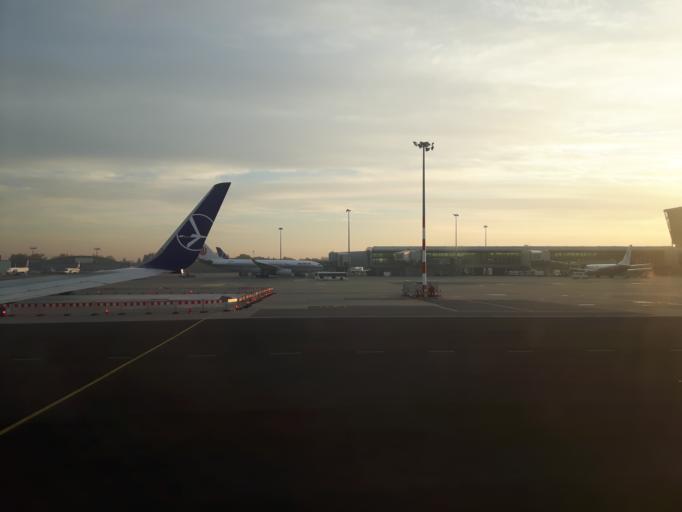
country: PL
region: Masovian Voivodeship
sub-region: Warszawa
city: Wlochy
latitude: 52.1734
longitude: 20.9645
